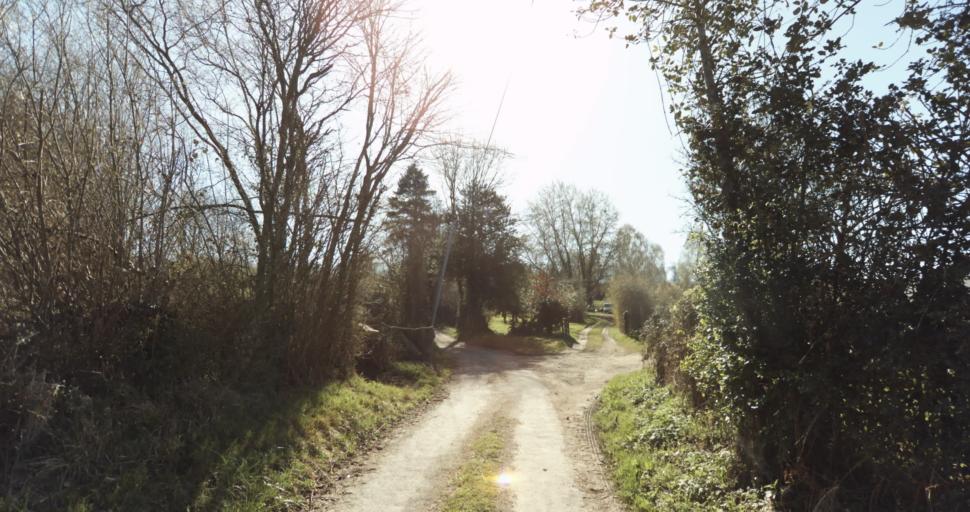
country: FR
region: Lower Normandy
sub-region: Departement du Calvados
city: Livarot
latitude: 48.9866
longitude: 0.0646
